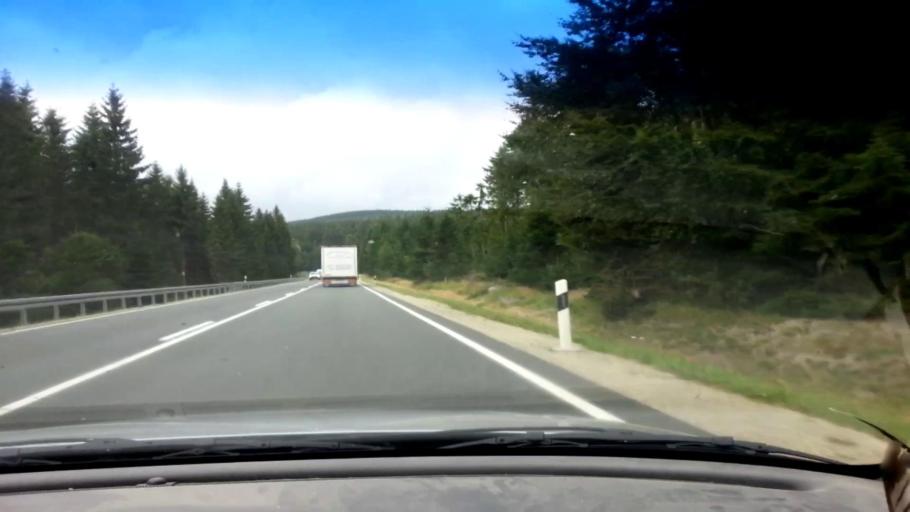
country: DE
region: Bavaria
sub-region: Upper Franconia
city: Fichtelberg
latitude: 50.0148
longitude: 11.8785
